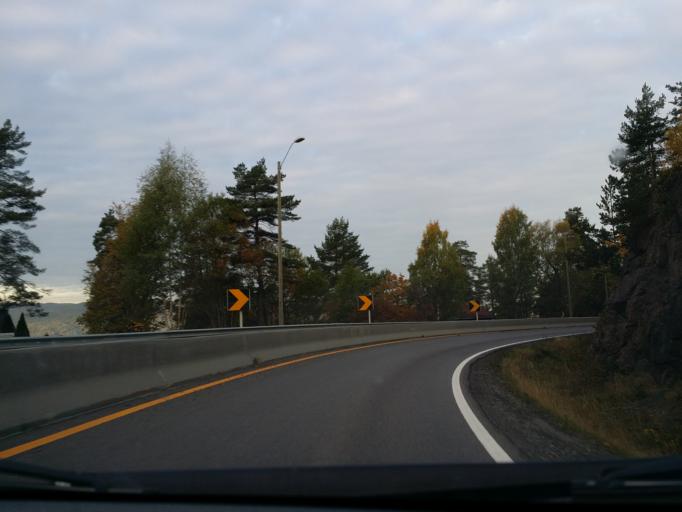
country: NO
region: Buskerud
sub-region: Hole
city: Vik
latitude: 59.9721
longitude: 10.3349
